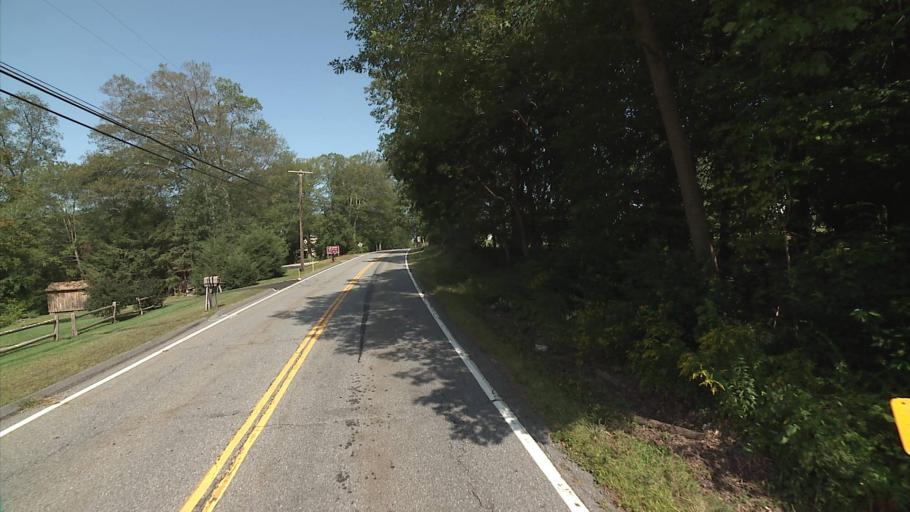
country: US
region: Connecticut
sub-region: Windham County
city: South Woodstock
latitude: 41.9706
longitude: -71.9893
